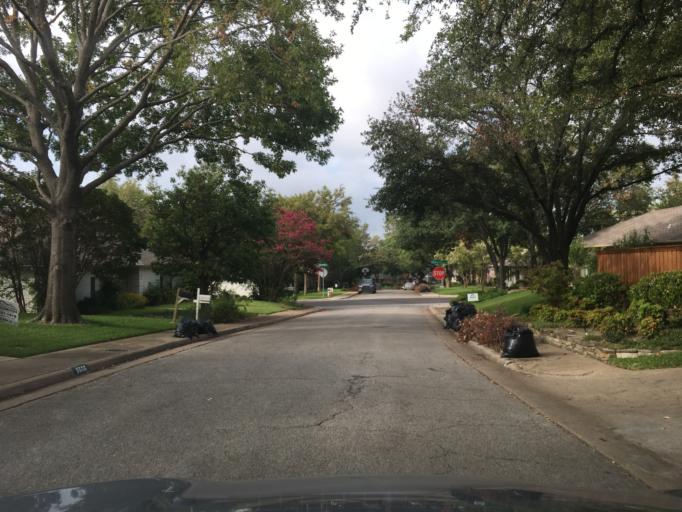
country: US
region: Texas
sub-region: Dallas County
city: Richardson
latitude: 32.8978
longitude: -96.7486
